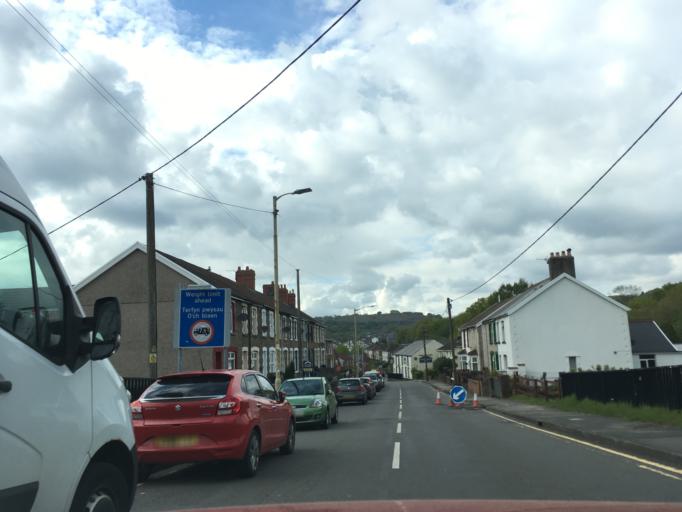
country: GB
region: Wales
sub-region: Caerphilly County Borough
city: Nelson
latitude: 51.6627
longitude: -3.2926
